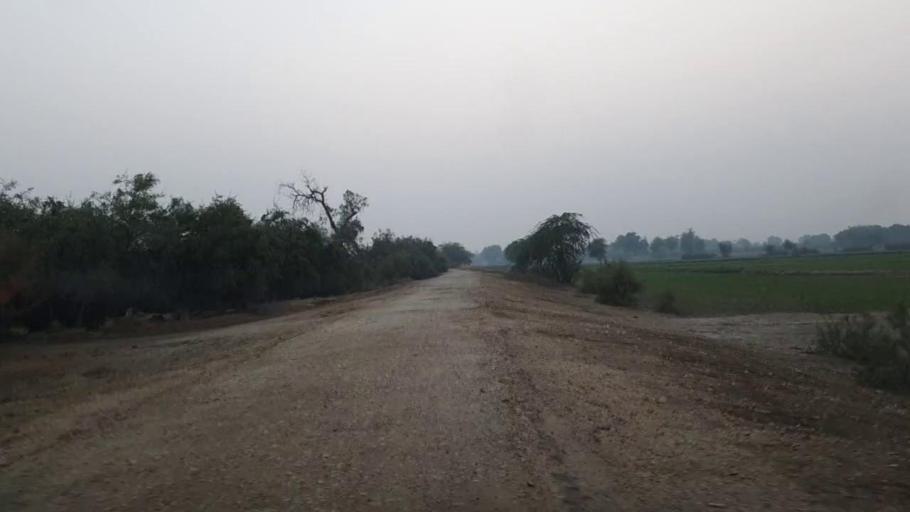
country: PK
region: Sindh
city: Karaundi
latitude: 26.9532
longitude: 68.4536
